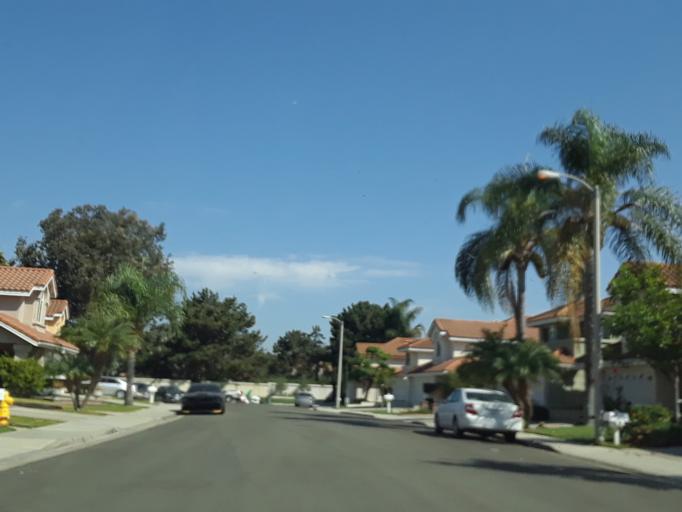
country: US
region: California
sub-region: Orange County
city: Irvine
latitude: 33.6774
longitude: -117.8207
